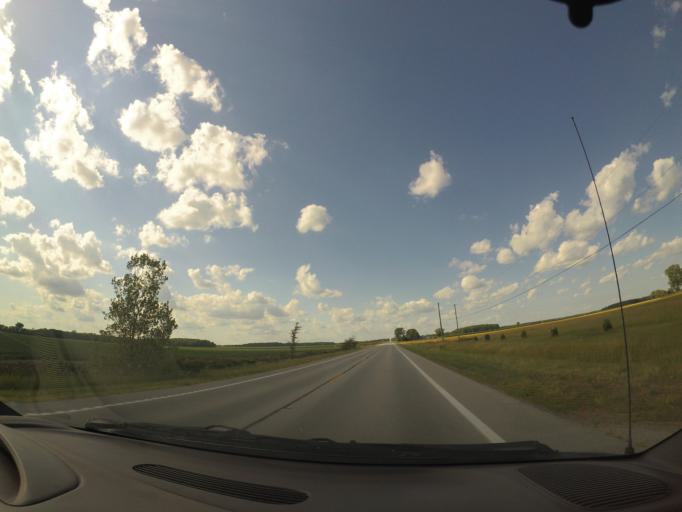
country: US
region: Ohio
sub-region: Wood County
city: Pemberville
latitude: 41.3884
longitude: -83.4163
